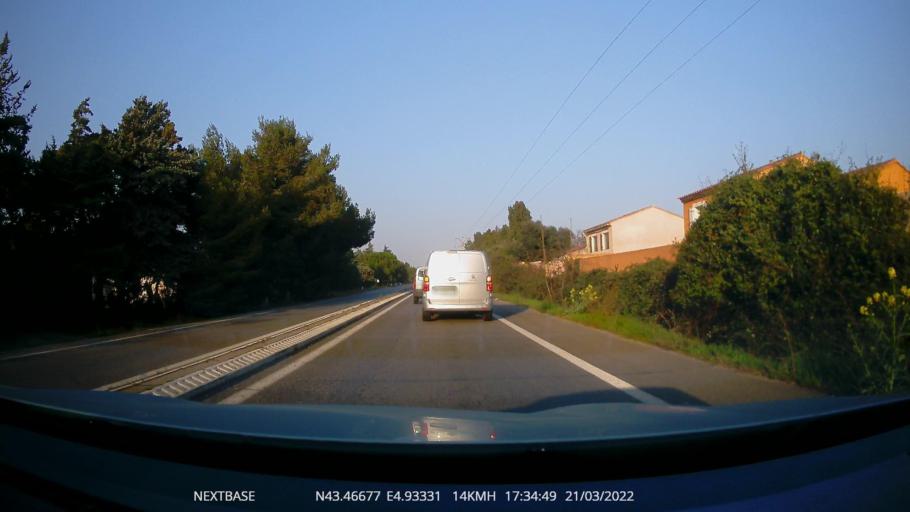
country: FR
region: Provence-Alpes-Cote d'Azur
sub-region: Departement des Bouches-du-Rhone
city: Fos-sur-Mer
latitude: 43.4668
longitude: 4.9333
